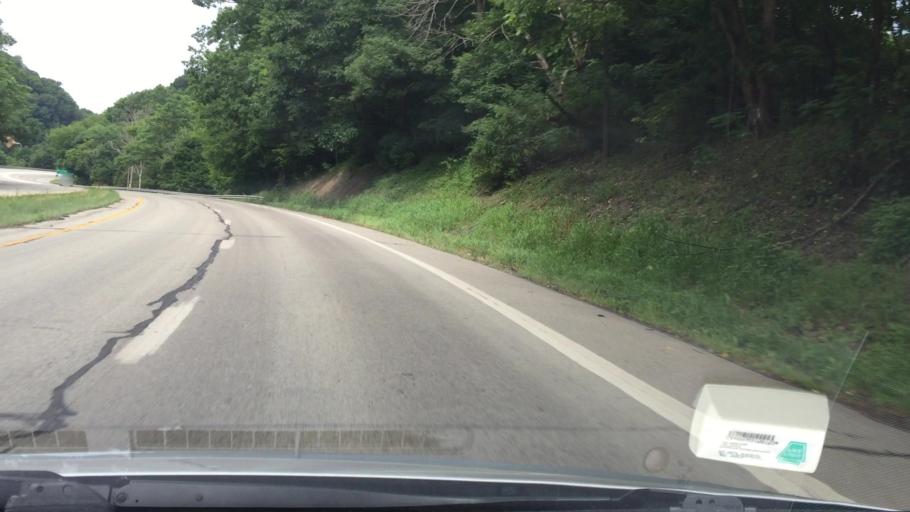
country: US
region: Pennsylvania
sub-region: Westmoreland County
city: New Kensington
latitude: 40.5765
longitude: -79.7402
